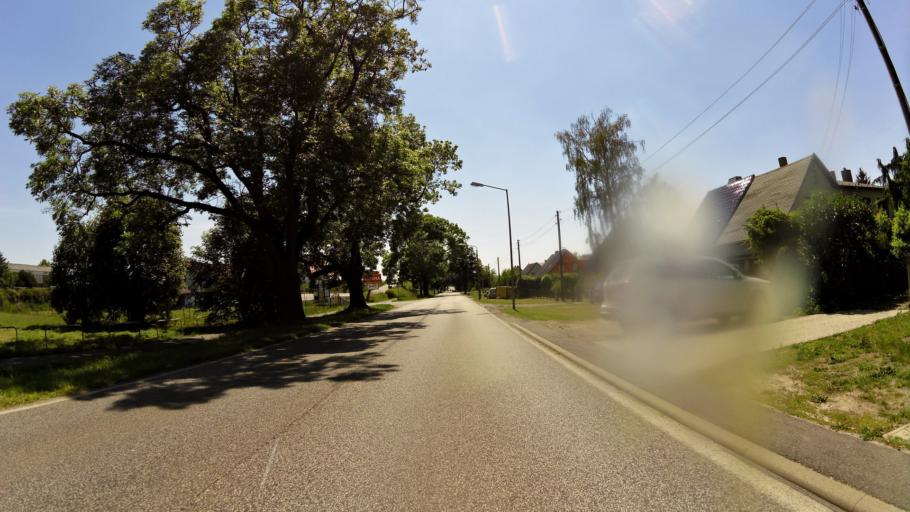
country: DE
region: Brandenburg
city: Lebus
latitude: 52.4189
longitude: 14.5293
